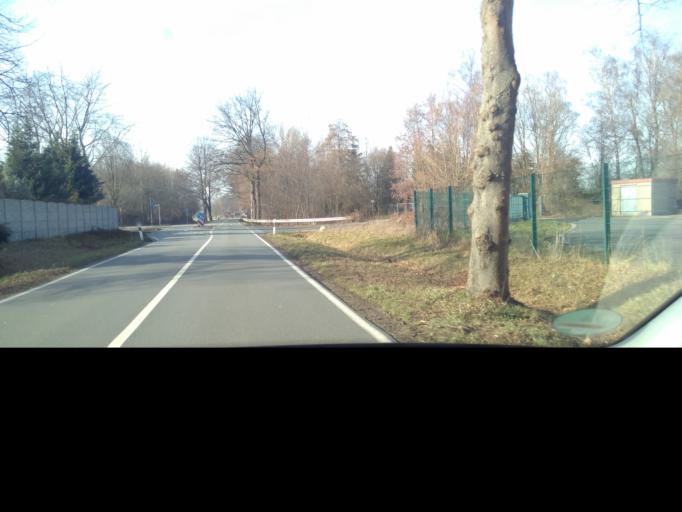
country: DE
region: North Rhine-Westphalia
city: Rietberg
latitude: 51.8380
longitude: 8.4348
